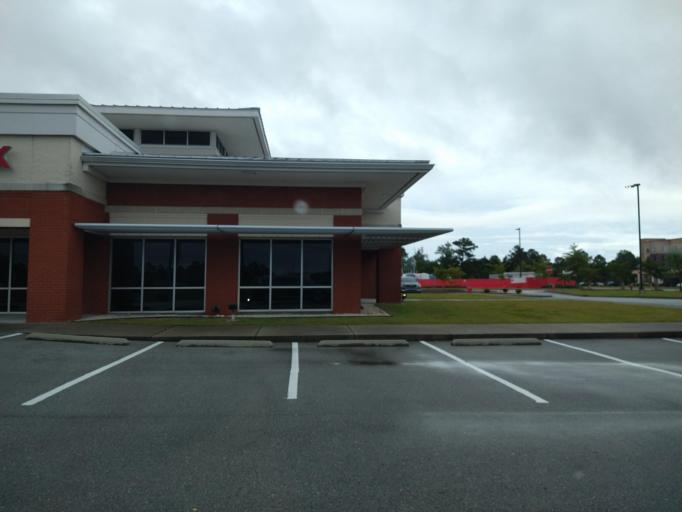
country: US
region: North Carolina
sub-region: Onslow County
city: Pumpkin Center
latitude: 34.7974
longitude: -77.4109
